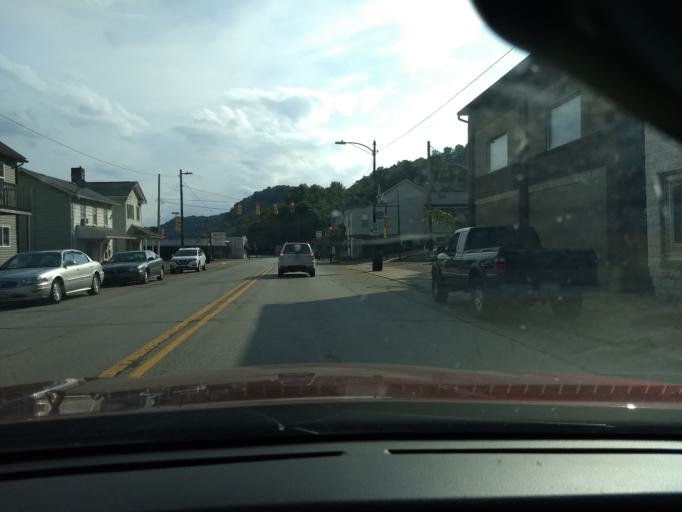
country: US
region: Pennsylvania
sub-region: Allegheny County
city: Tarentum
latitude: 40.5985
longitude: -79.7642
